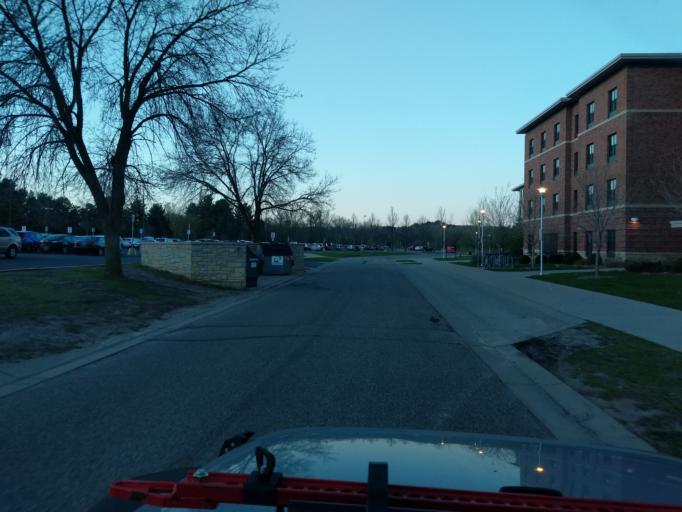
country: US
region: Wisconsin
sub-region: Pierce County
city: River Falls
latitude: 44.8518
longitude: -92.6143
